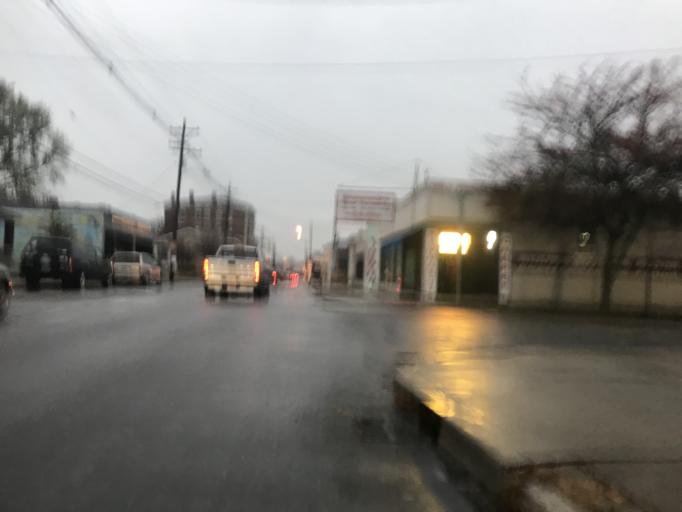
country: US
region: Kentucky
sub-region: Jefferson County
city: Louisville
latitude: 38.2320
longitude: -85.7418
